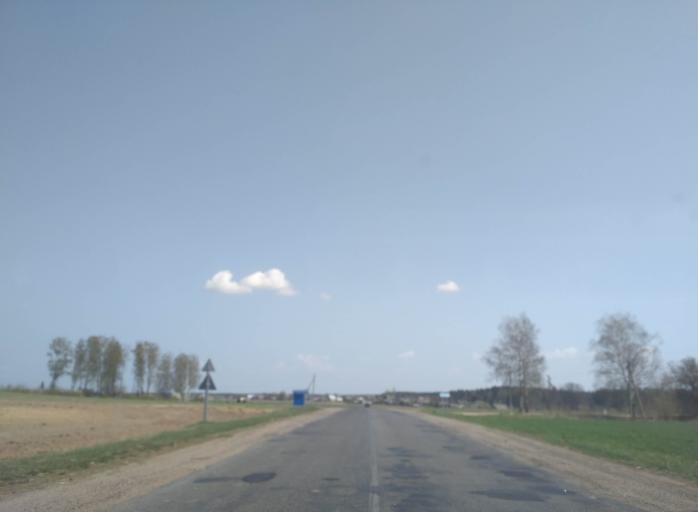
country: BY
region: Minsk
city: Horad Barysaw
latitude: 54.3151
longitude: 28.5571
